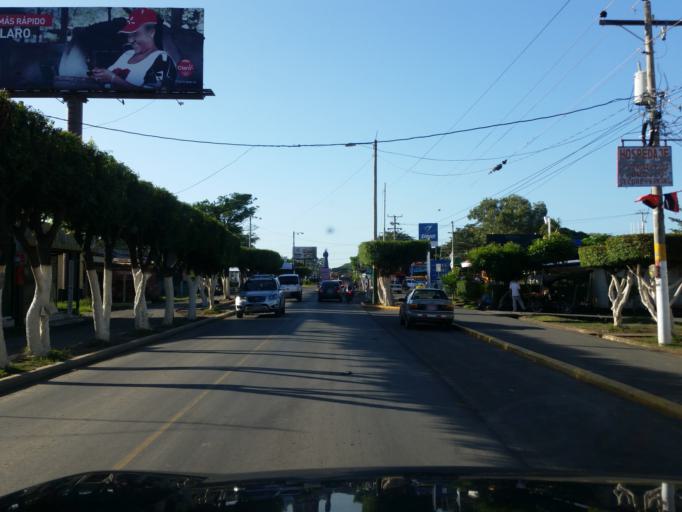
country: NI
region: Rivas
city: Rivas
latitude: 11.4435
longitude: -85.8261
